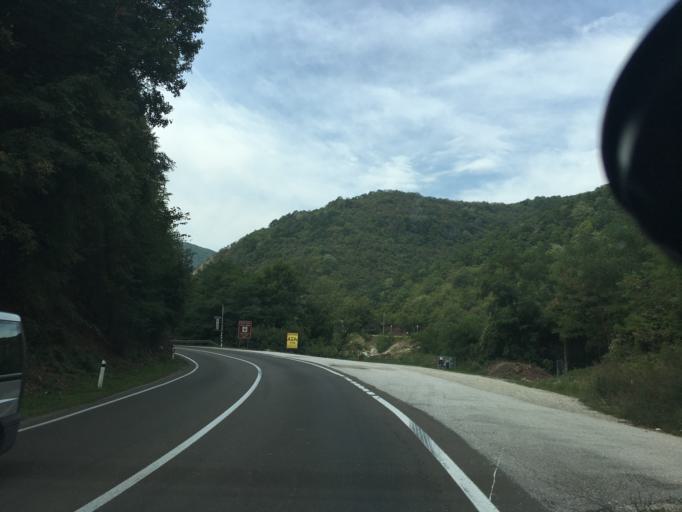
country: RS
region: Central Serbia
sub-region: Moravicki Okrug
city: Lucani
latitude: 43.9048
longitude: 20.1966
